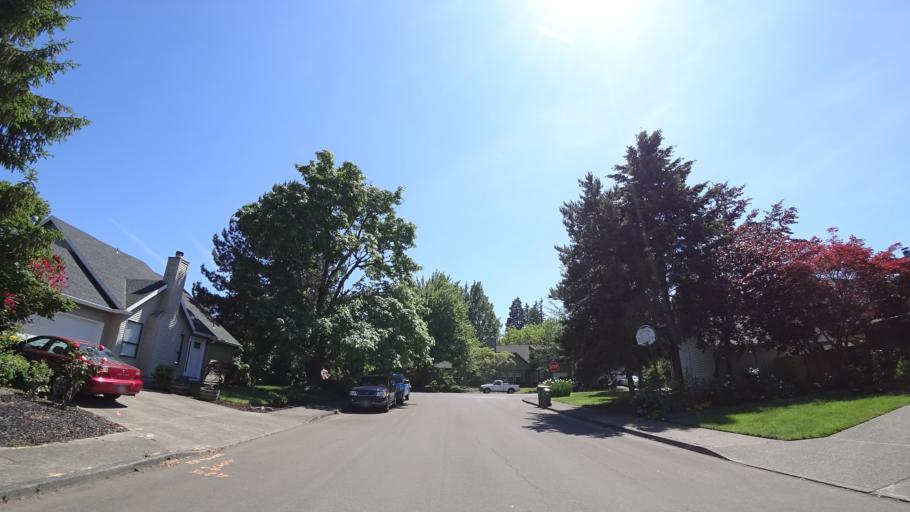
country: US
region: Oregon
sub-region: Washington County
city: King City
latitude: 45.4366
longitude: -122.8150
